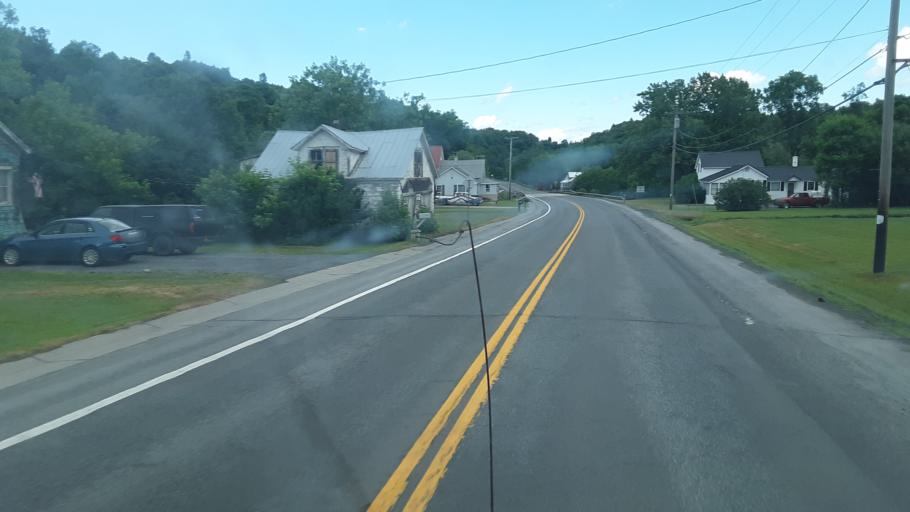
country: US
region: New York
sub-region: Oneida County
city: Rome
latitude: 43.3666
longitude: -75.4811
